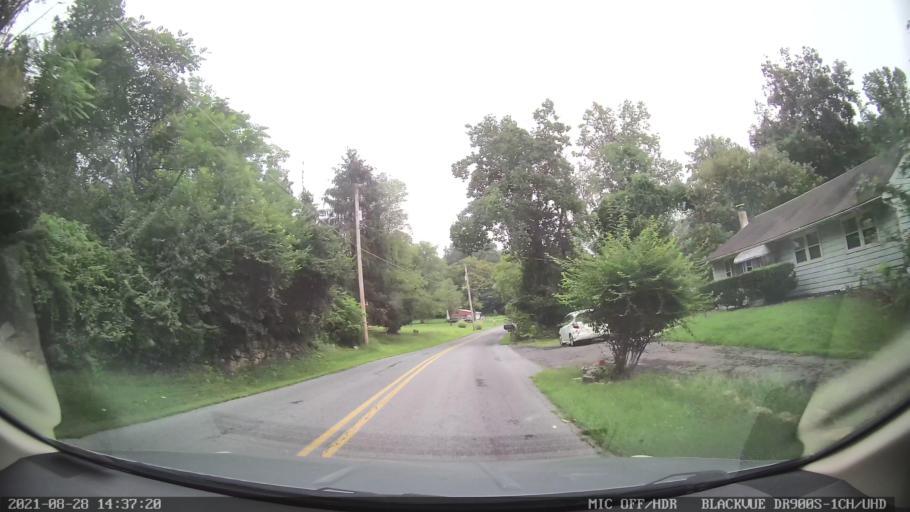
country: US
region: Pennsylvania
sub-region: Berks County
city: South Temple
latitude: 40.3873
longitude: -75.8675
